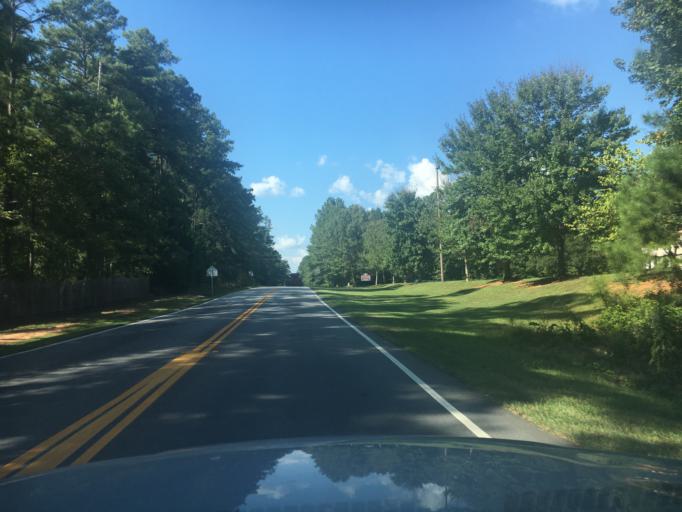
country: US
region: South Carolina
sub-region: Greenwood County
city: Greenwood
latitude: 34.2351
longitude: -82.1791
